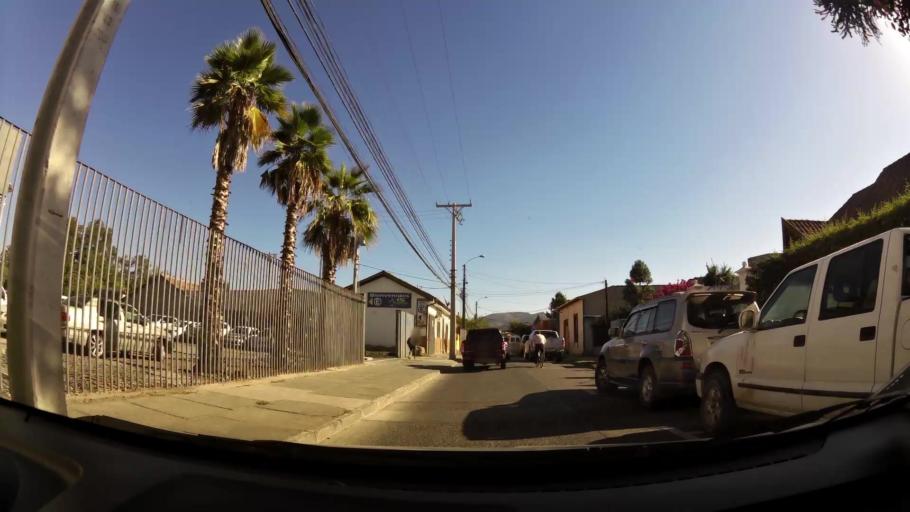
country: CL
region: O'Higgins
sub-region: Provincia de Colchagua
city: Chimbarongo
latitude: -34.5883
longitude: -70.9915
